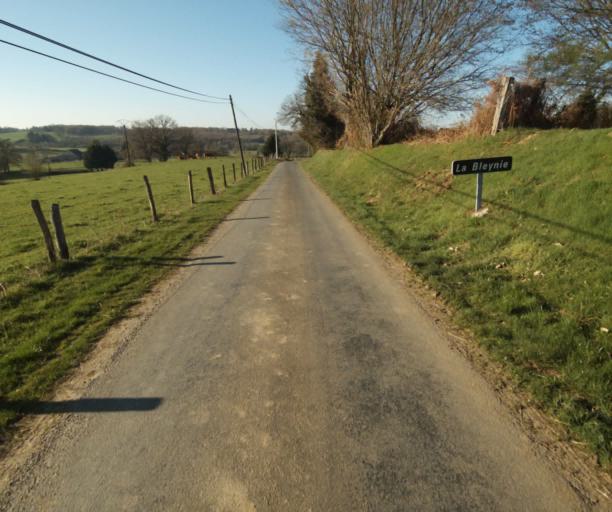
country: FR
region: Limousin
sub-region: Departement de la Correze
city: Uzerche
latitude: 45.3849
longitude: 1.5878
